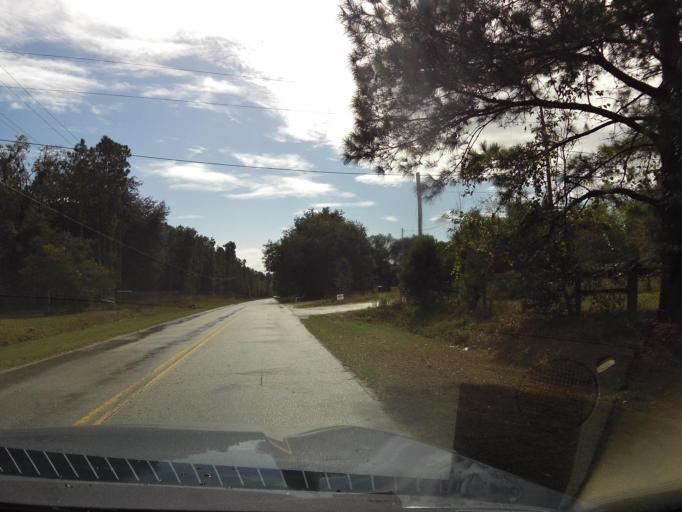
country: US
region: Florida
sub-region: Clay County
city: Asbury Lake
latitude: 30.0085
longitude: -81.8435
